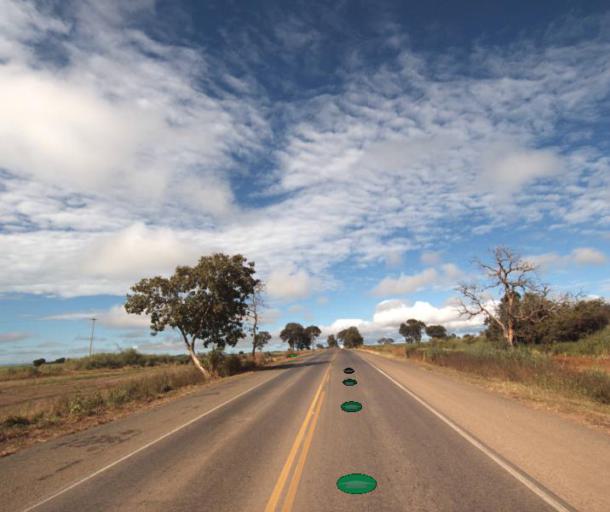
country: BR
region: Goias
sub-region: Uruacu
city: Uruacu
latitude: -14.6782
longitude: -49.2043
